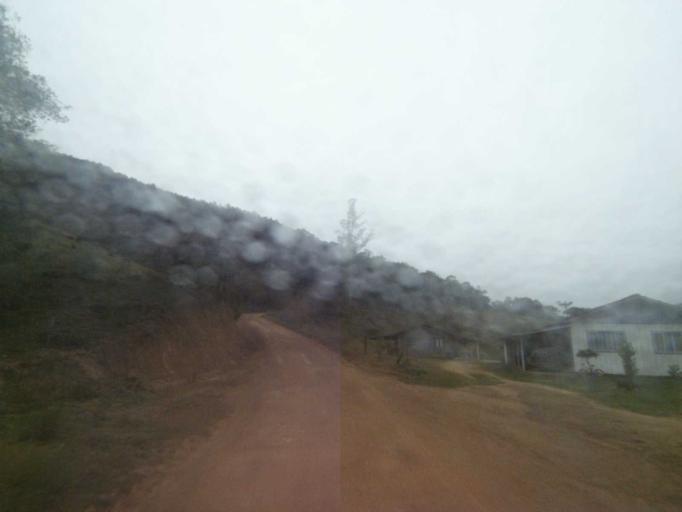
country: BR
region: Santa Catarina
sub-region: Anitapolis
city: Anitapolis
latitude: -27.8823
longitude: -49.1331
